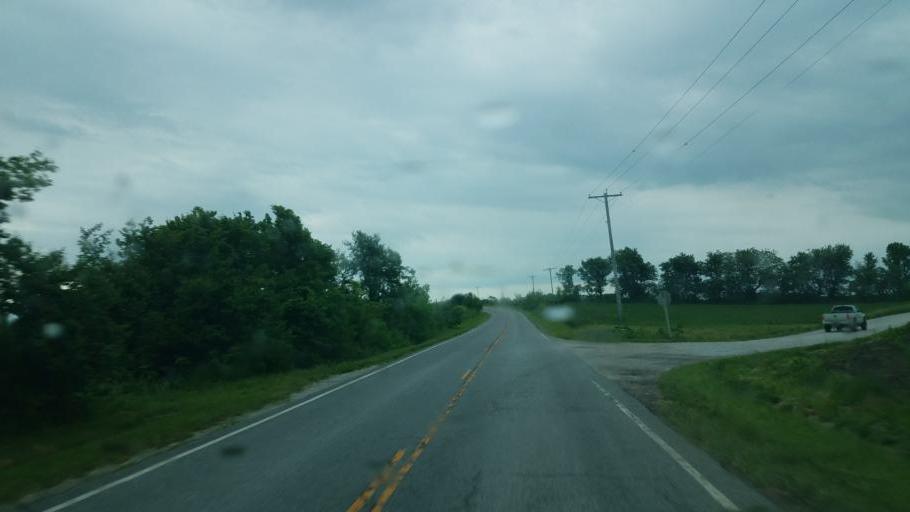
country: US
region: Missouri
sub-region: Cooper County
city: Boonville
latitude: 38.8383
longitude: -92.6226
